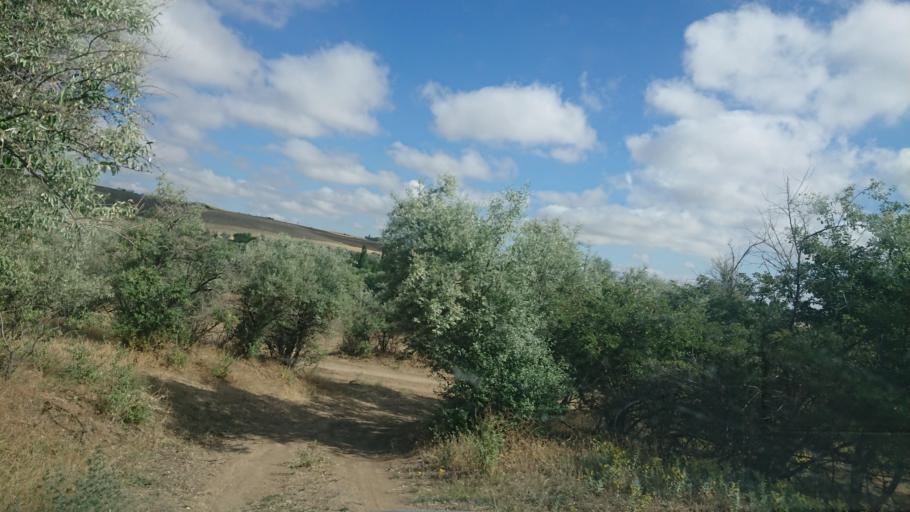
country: TR
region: Aksaray
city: Agacoren
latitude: 38.8518
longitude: 33.9350
